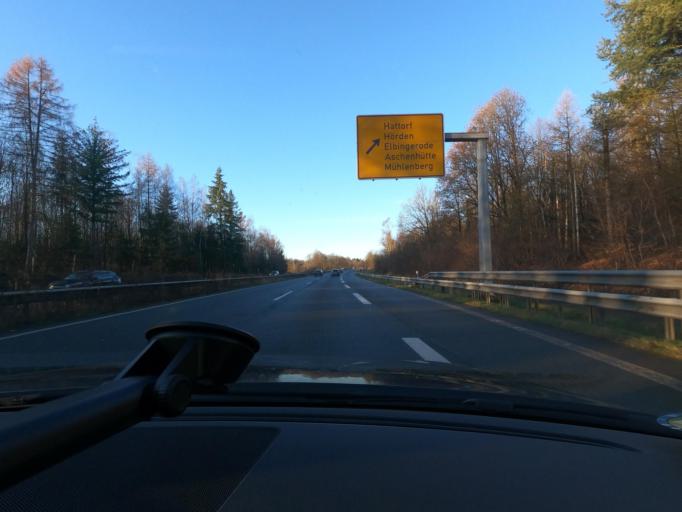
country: DE
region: Lower Saxony
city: Hoerden
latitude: 51.6730
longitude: 10.3123
